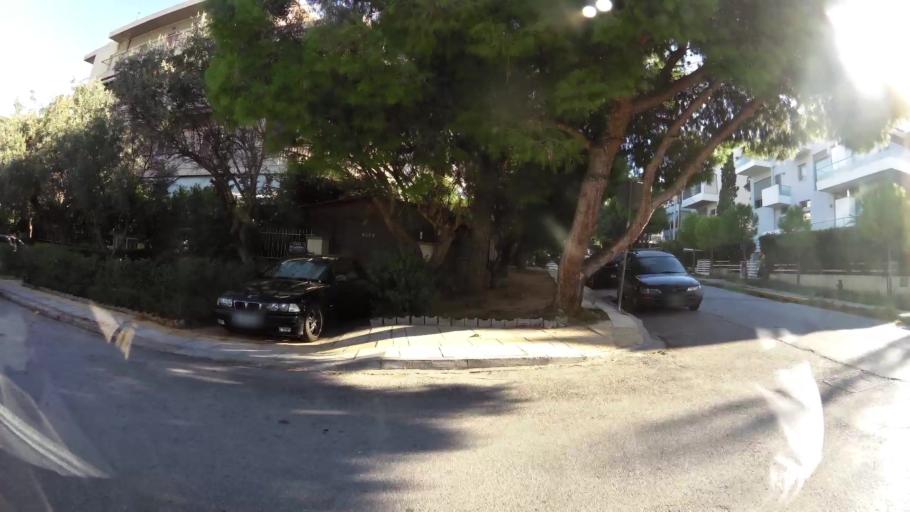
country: GR
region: Attica
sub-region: Nomarchia Athinas
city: Glyfada
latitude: 37.8585
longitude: 23.7678
